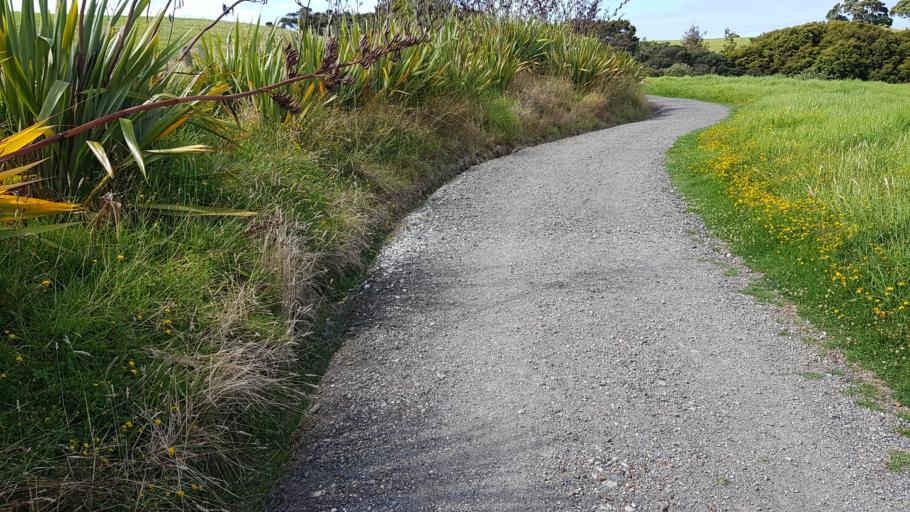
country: NZ
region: Auckland
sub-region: Auckland
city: Rothesay Bay
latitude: -36.6726
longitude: 174.7458
